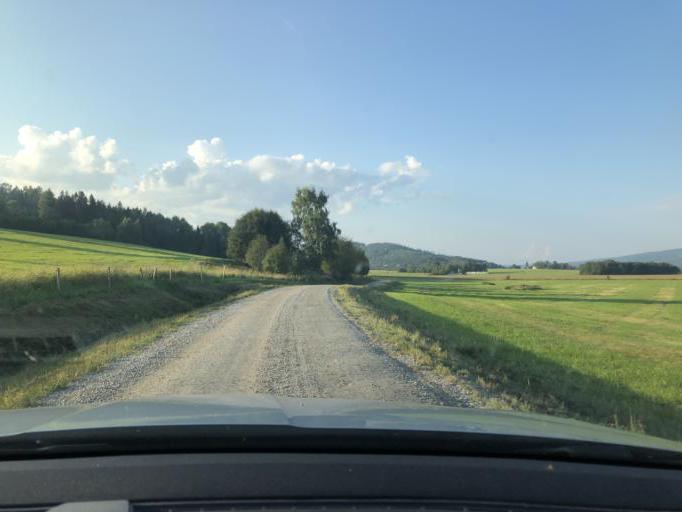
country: SE
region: Vaesternorrland
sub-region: Kramfors Kommun
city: Bollstabruk
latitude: 63.0661
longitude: 17.7347
